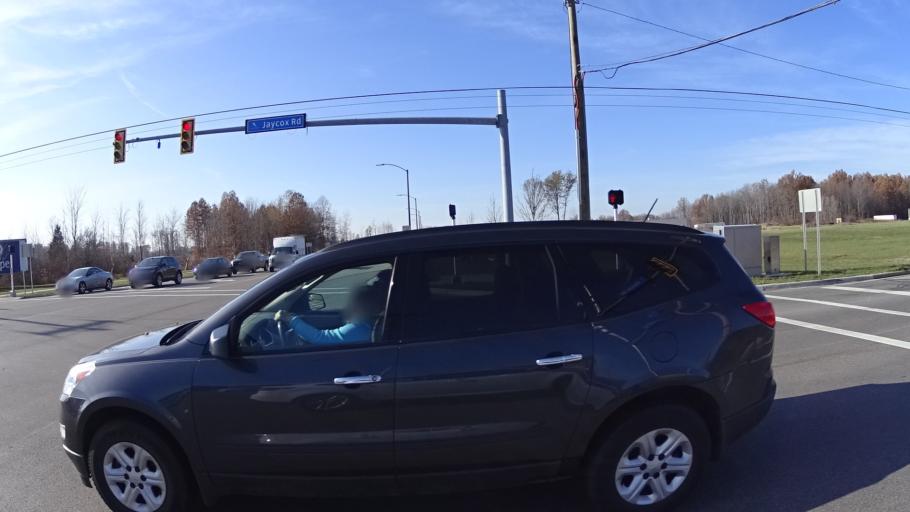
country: US
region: Ohio
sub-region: Lorain County
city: Avon Center
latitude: 41.4676
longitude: -81.9996
